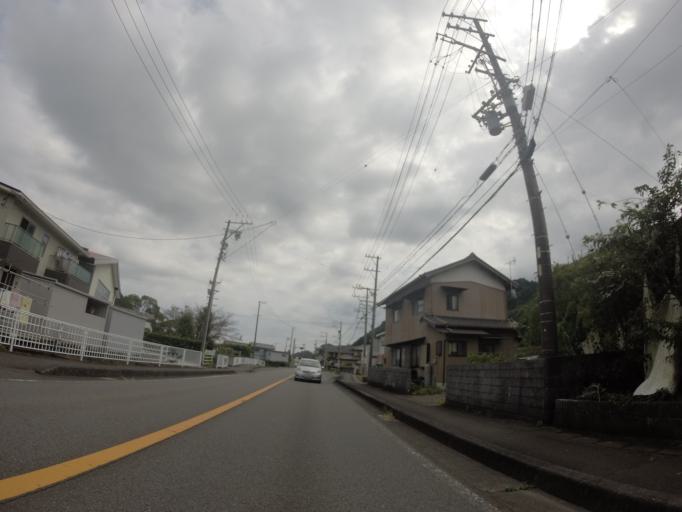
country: JP
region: Shizuoka
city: Fujieda
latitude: 34.8817
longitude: 138.2170
